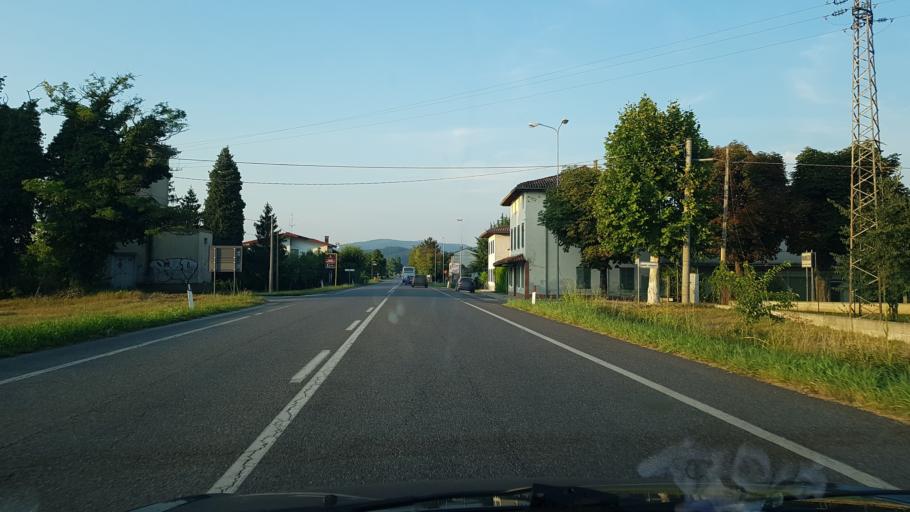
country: IT
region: Friuli Venezia Giulia
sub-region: Provincia di Gorizia
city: Savogna d'Isonzo
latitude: 45.9081
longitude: 13.5528
